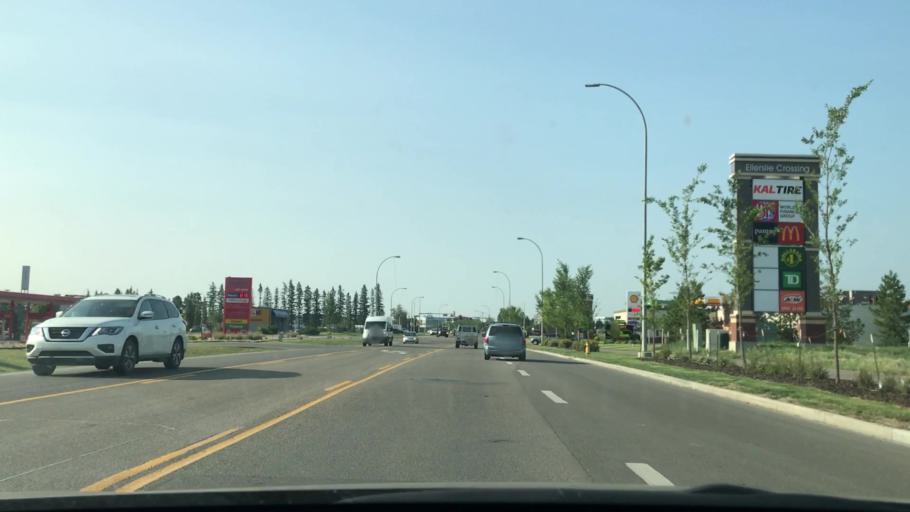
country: CA
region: Alberta
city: Beaumont
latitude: 53.4277
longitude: -113.4800
